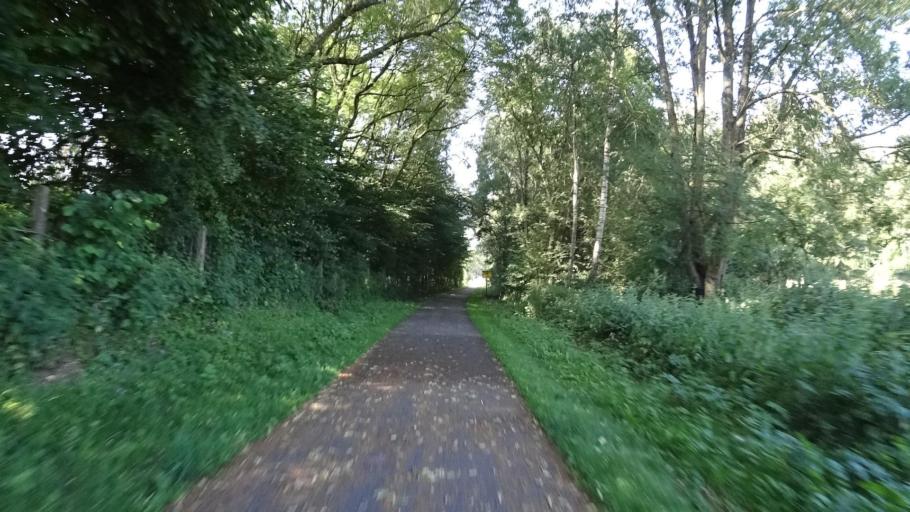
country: BE
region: Wallonia
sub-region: Province de Namur
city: Namur
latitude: 50.5107
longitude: 4.8703
